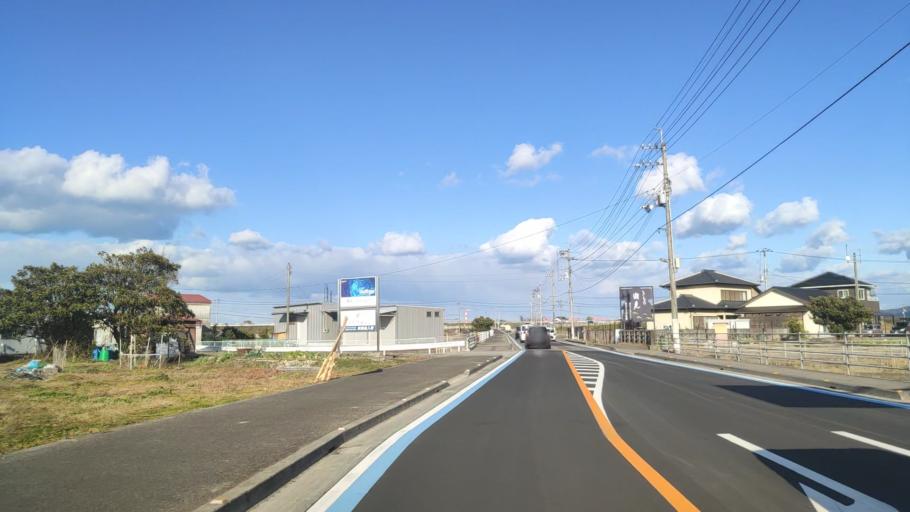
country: JP
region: Ehime
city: Saijo
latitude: 33.9092
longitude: 133.1571
